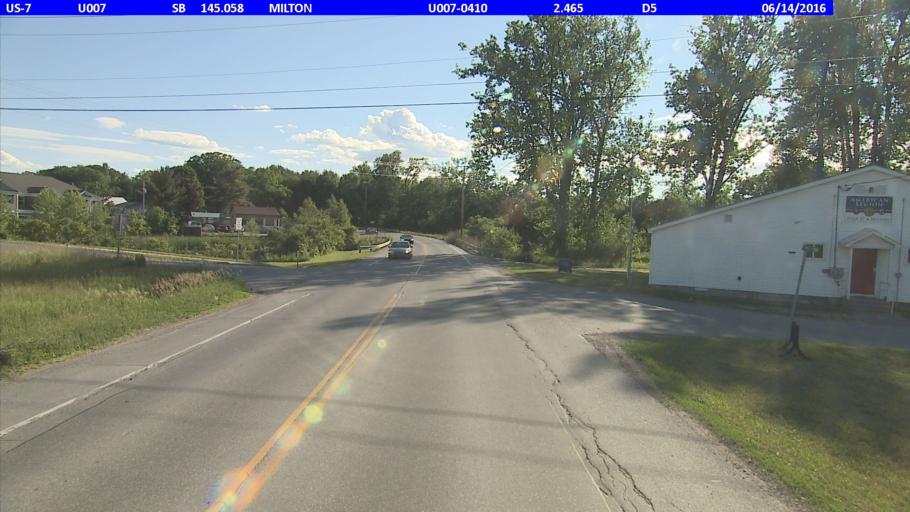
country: US
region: Vermont
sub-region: Chittenden County
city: Milton
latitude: 44.6275
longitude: -73.1441
